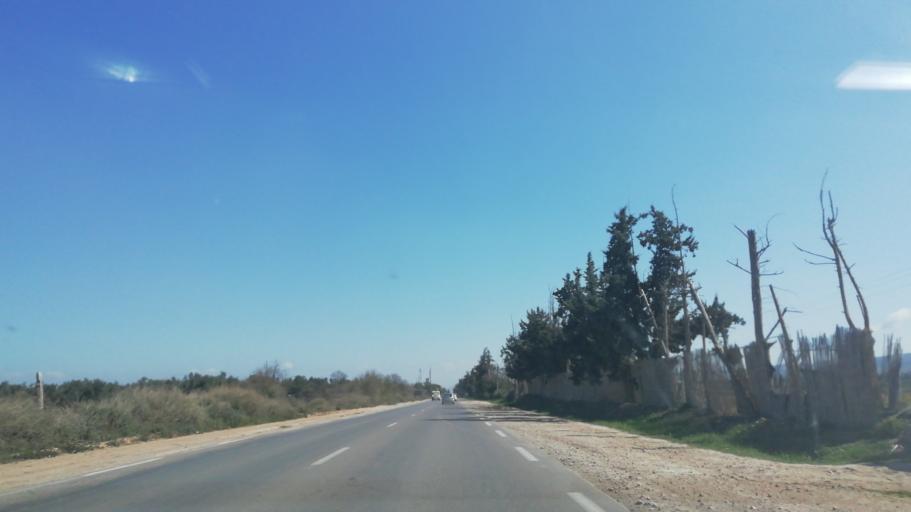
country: DZ
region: Mascara
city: Sig
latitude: 35.5693
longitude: -0.0497
